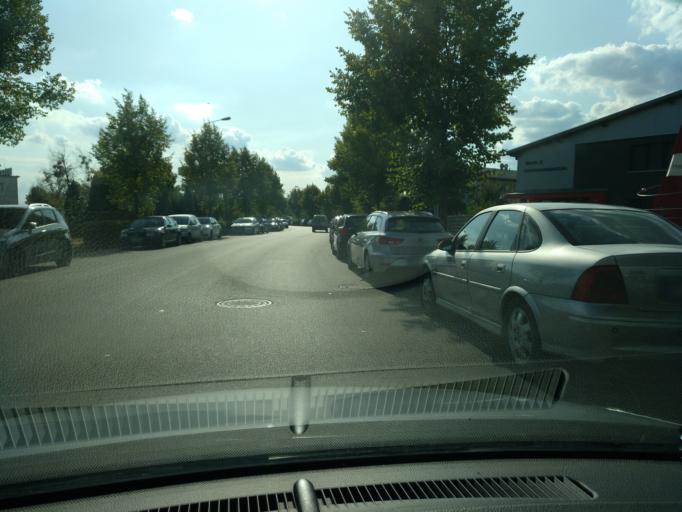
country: DE
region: Berlin
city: Mahlsdorf
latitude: 52.5061
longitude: 13.6348
